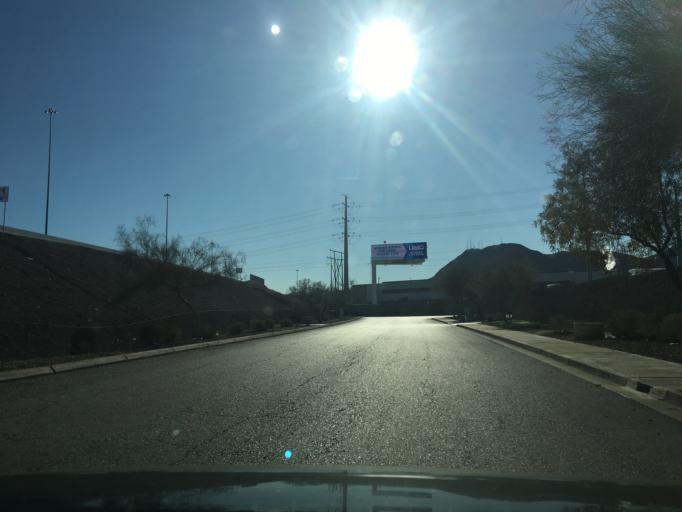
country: US
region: Nevada
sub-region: Clark County
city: Henderson
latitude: 36.0394
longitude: -115.0212
